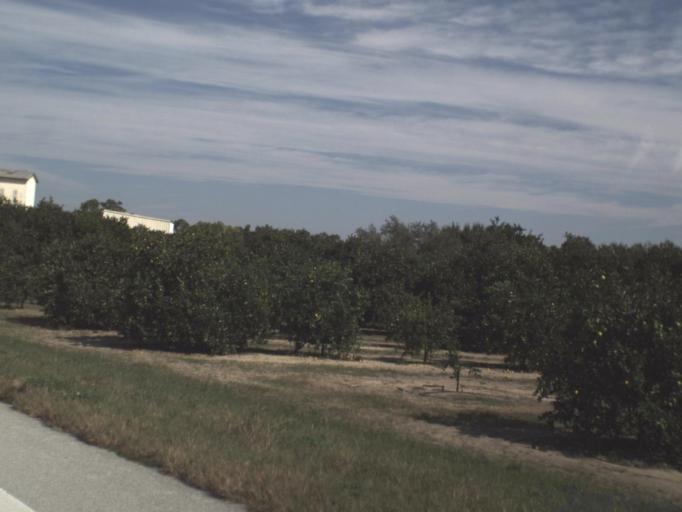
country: US
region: Florida
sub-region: Highlands County
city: Avon Park
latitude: 27.5799
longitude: -81.4662
